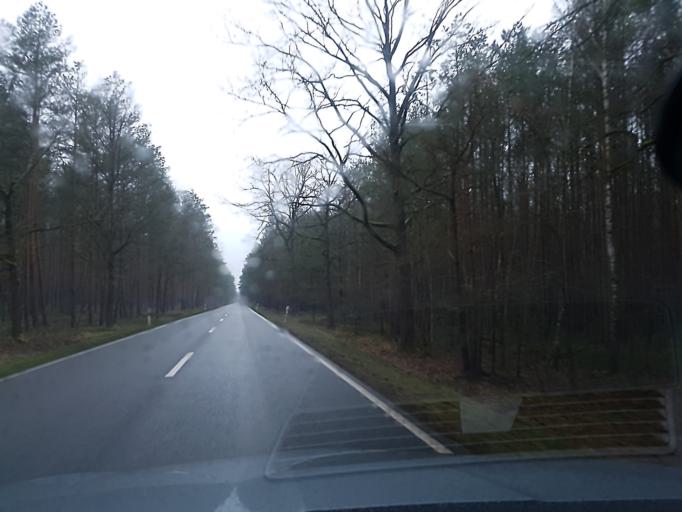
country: DE
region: Brandenburg
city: Schonborn
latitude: 51.6621
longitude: 13.4965
